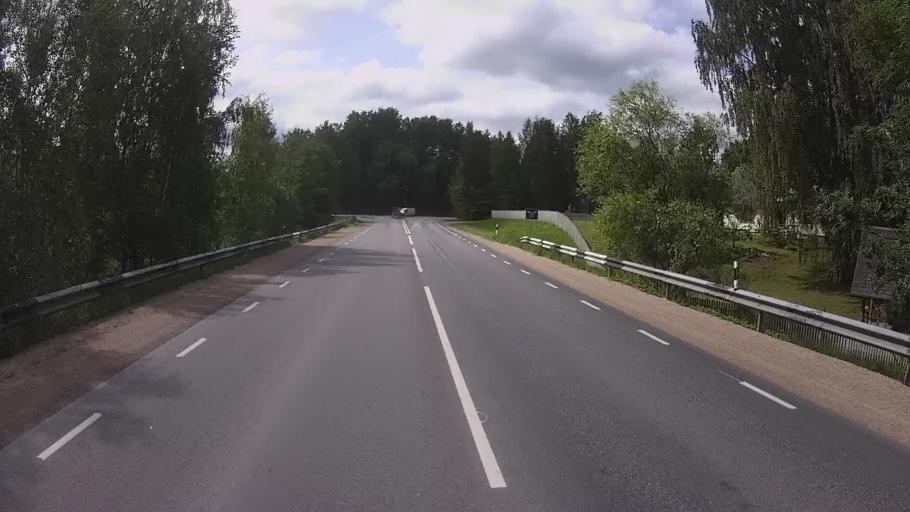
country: EE
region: Polvamaa
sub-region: Polva linn
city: Polva
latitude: 58.0437
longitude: 27.0722
